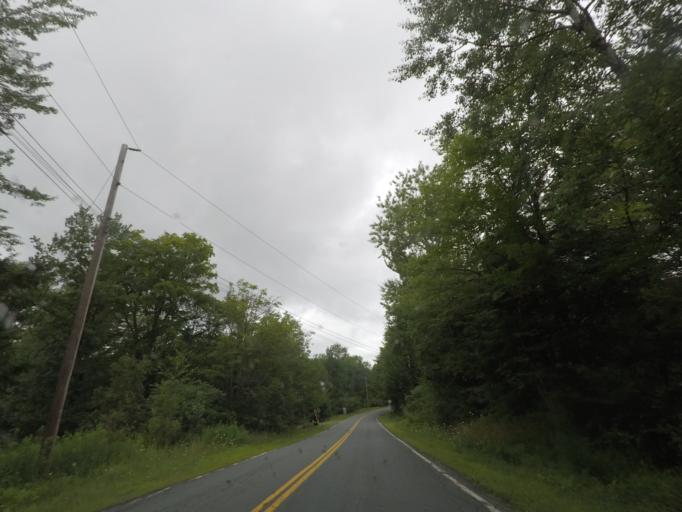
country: US
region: New York
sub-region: Rensselaer County
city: Poestenkill
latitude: 42.6880
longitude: -73.4427
